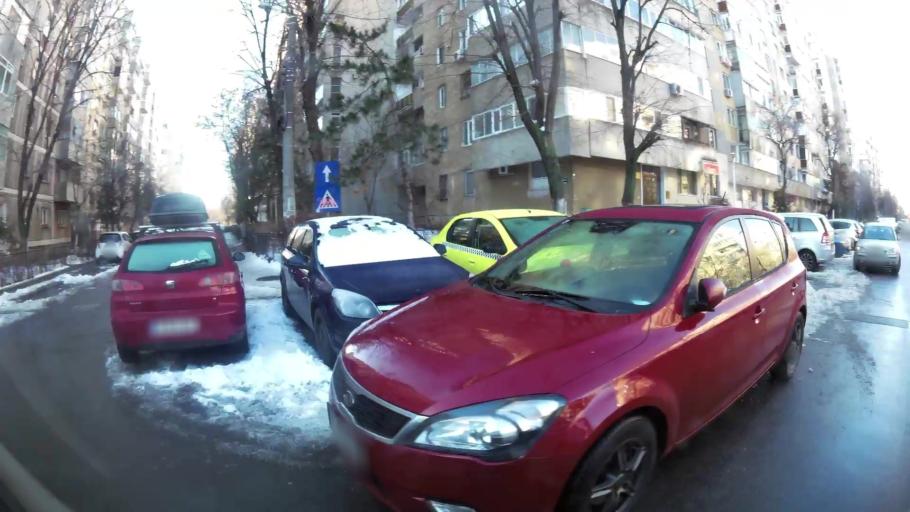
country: RO
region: Bucuresti
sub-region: Municipiul Bucuresti
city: Bucharest
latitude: 44.4119
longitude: 26.1120
